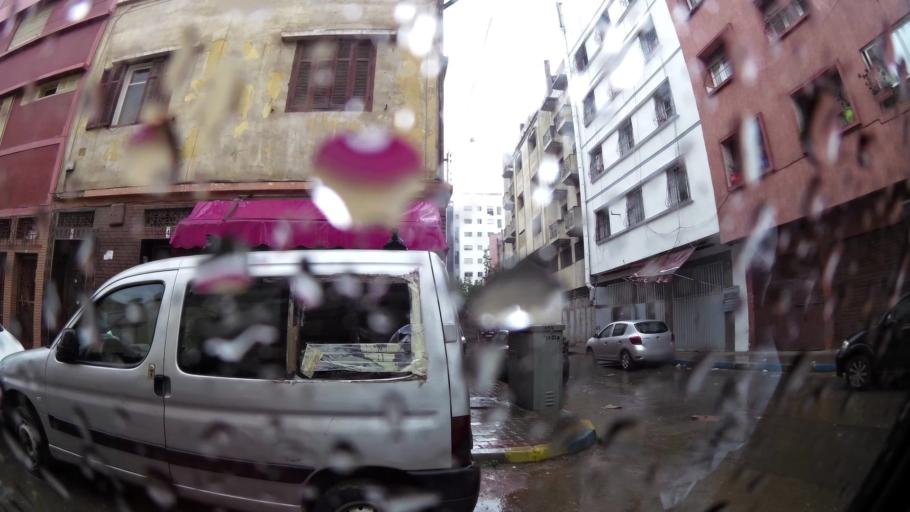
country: MA
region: Grand Casablanca
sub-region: Casablanca
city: Casablanca
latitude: 33.5719
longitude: -7.5948
